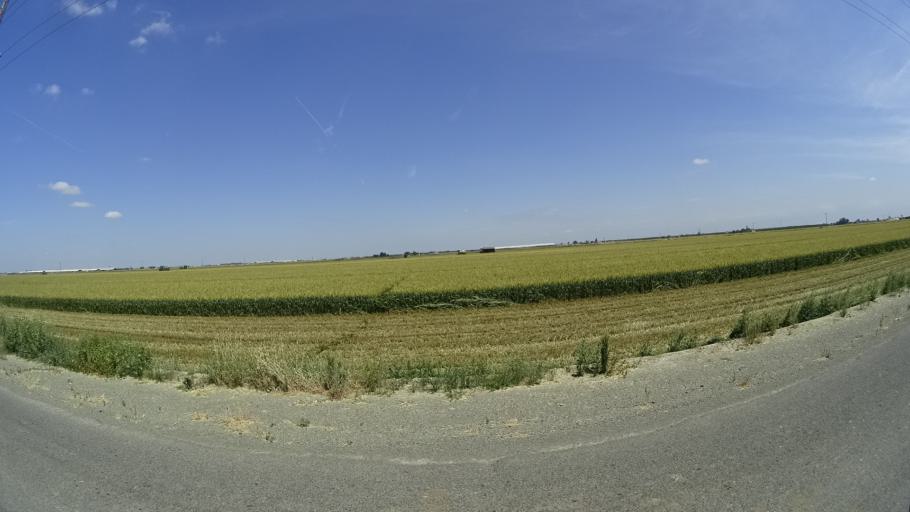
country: US
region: California
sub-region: Tulare County
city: Goshen
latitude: 36.3136
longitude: -119.5011
